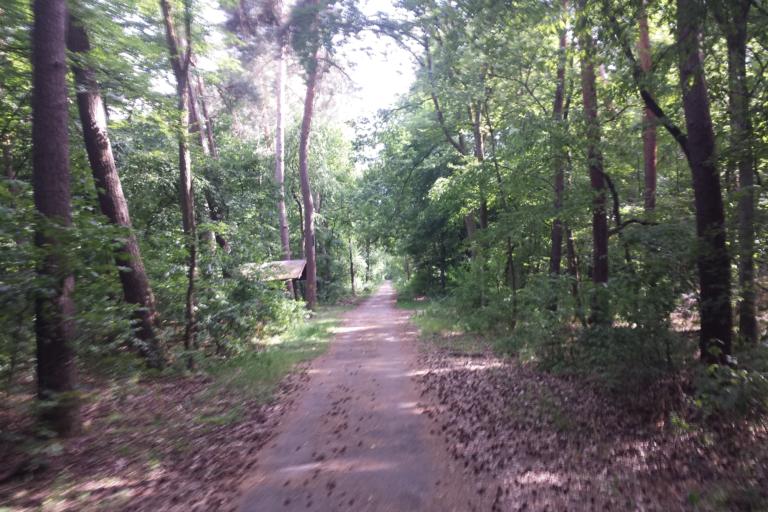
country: DE
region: Hesse
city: Viernheim
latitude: 49.5398
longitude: 8.5237
